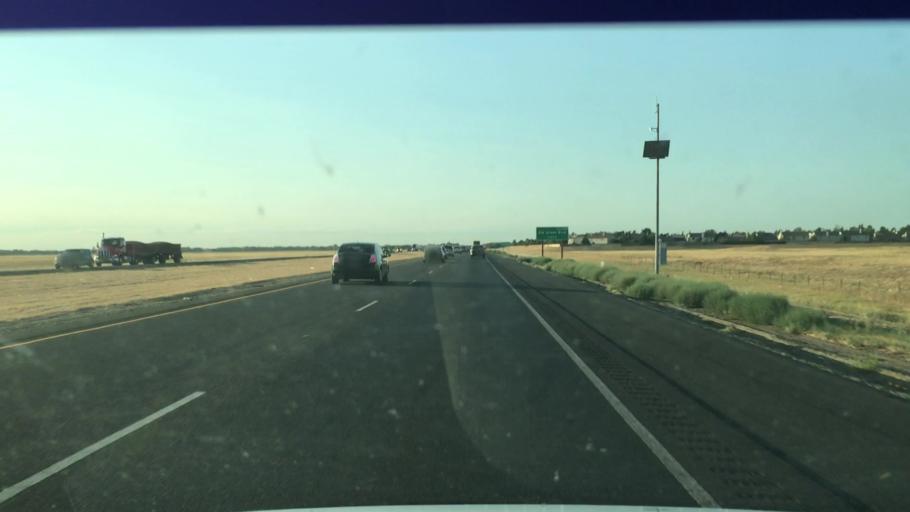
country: US
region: California
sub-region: Sacramento County
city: Laguna
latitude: 38.3897
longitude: -121.4796
